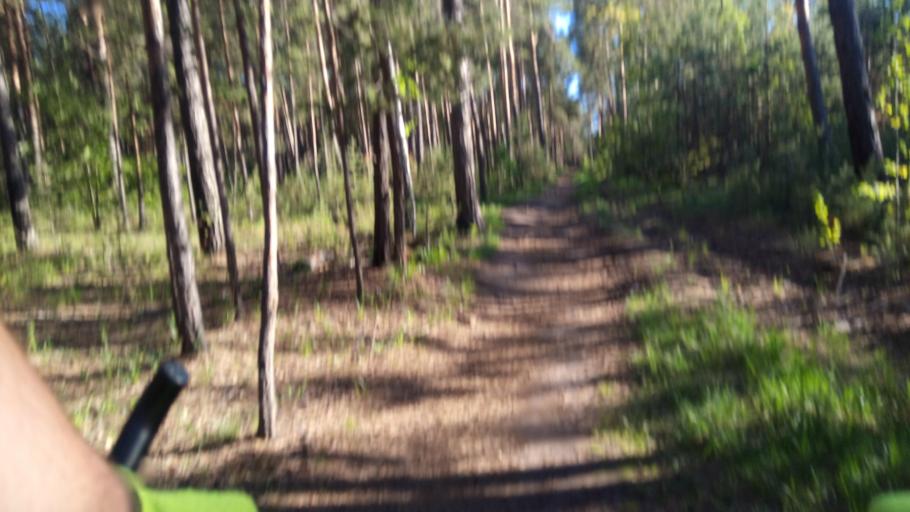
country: RU
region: Chelyabinsk
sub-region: Gorod Chelyabinsk
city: Chelyabinsk
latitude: 55.1350
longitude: 61.3355
